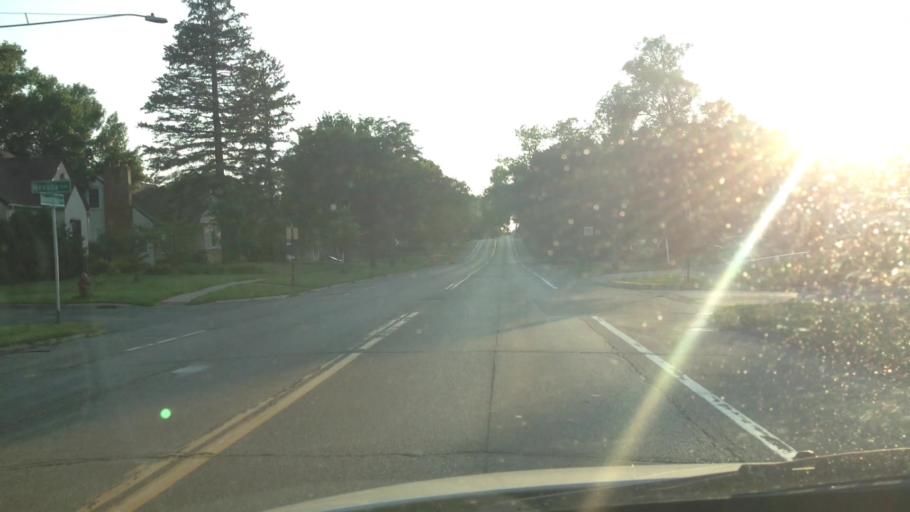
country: US
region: Minnesota
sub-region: Hennepin County
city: Saint Louis Park
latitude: 44.9495
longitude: -93.3730
